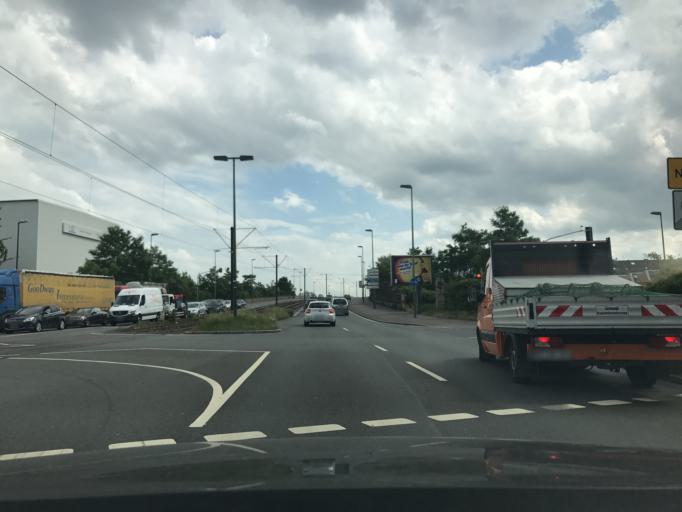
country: DE
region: North Rhine-Westphalia
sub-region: Regierungsbezirk Dusseldorf
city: Neuss
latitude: 51.2253
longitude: 6.6983
